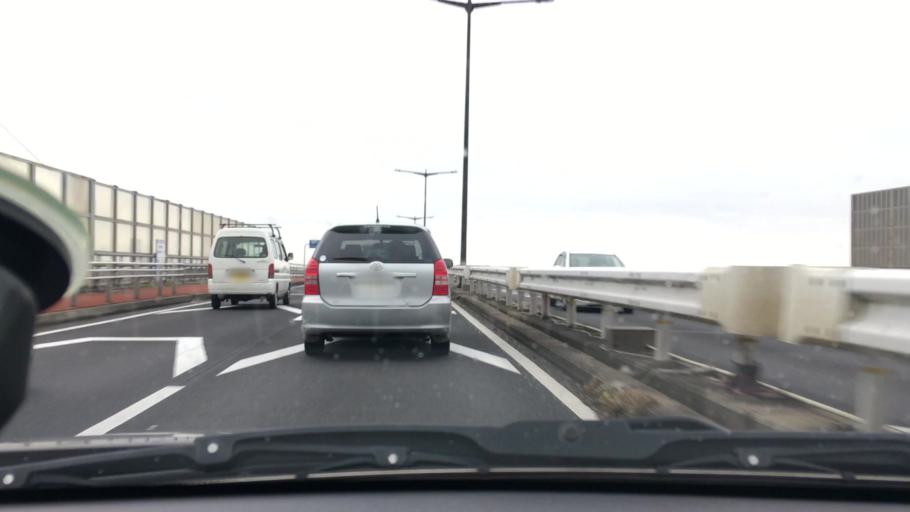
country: JP
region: Ibaraki
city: Kashima-shi
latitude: 35.9258
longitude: 140.6148
